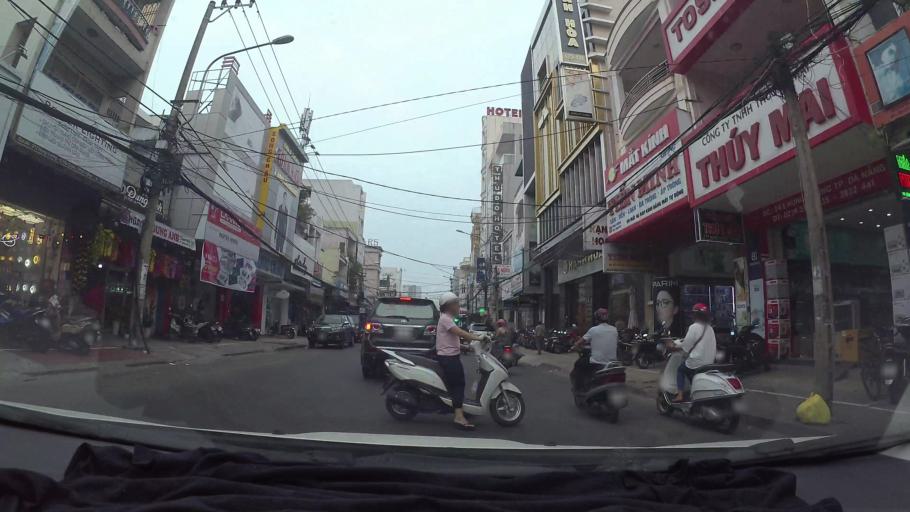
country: VN
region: Da Nang
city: Da Nang
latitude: 16.0678
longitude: 108.2169
